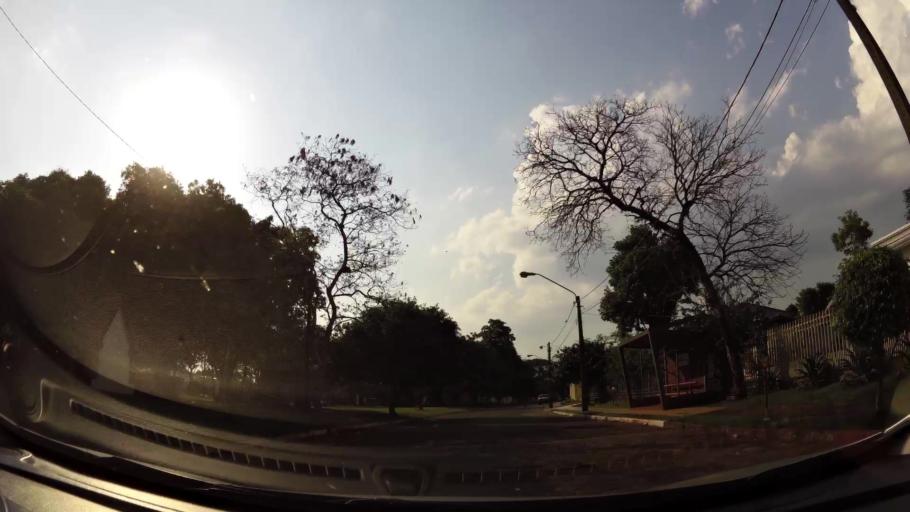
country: PY
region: Alto Parana
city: Presidente Franco
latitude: -25.5281
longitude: -54.6322
